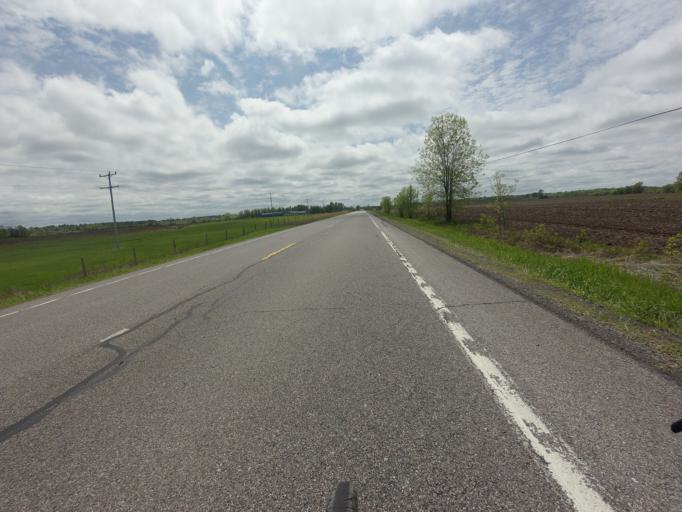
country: CA
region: Ontario
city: Cornwall
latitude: 44.9580
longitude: -74.6723
